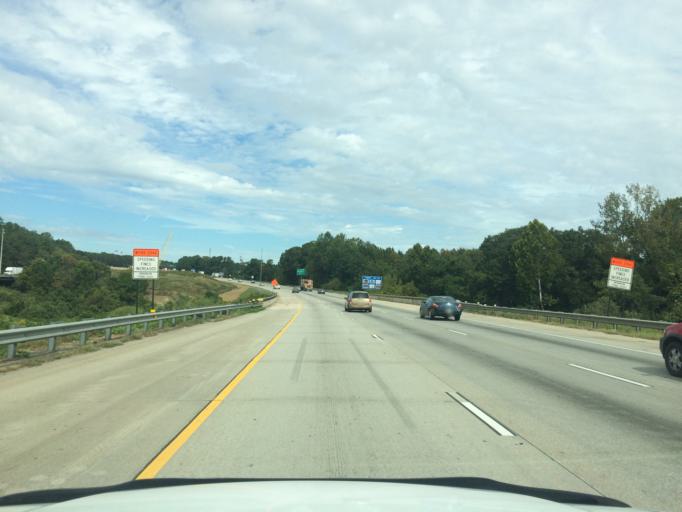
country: US
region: Georgia
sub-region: Cobb County
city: Kennesaw
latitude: 34.0202
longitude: -84.5699
